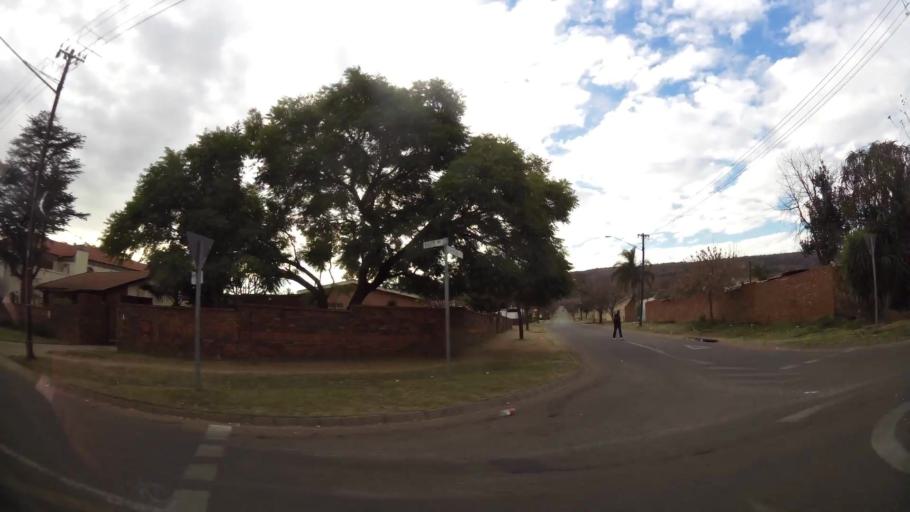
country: ZA
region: Gauteng
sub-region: City of Tshwane Metropolitan Municipality
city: Pretoria
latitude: -25.7041
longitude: 28.3127
